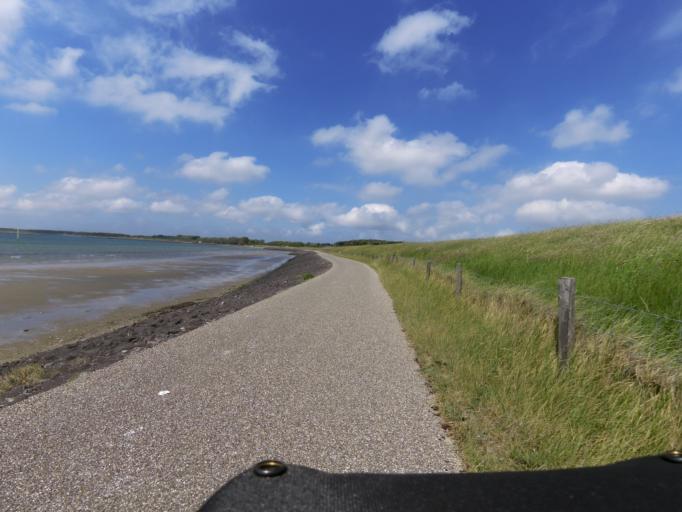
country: NL
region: Zeeland
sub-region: Schouwen-Duiveland
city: Scharendijke
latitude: 51.6941
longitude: 3.8213
